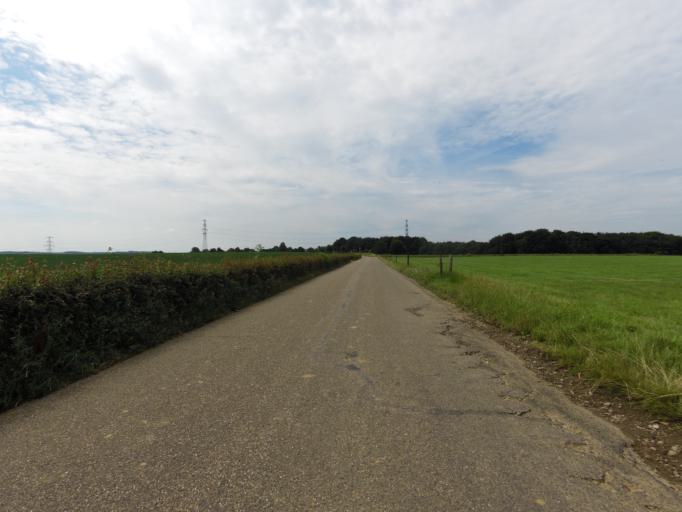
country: NL
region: Limburg
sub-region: Gemeente Voerendaal
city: Klimmen
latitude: 50.8725
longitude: 5.8737
